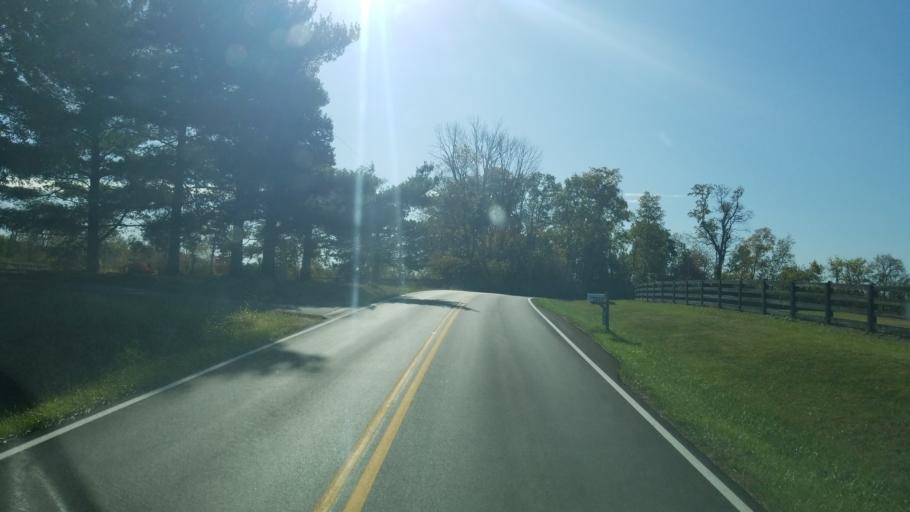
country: US
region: Ohio
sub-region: Warren County
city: Morrow
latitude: 39.3956
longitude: -84.0707
